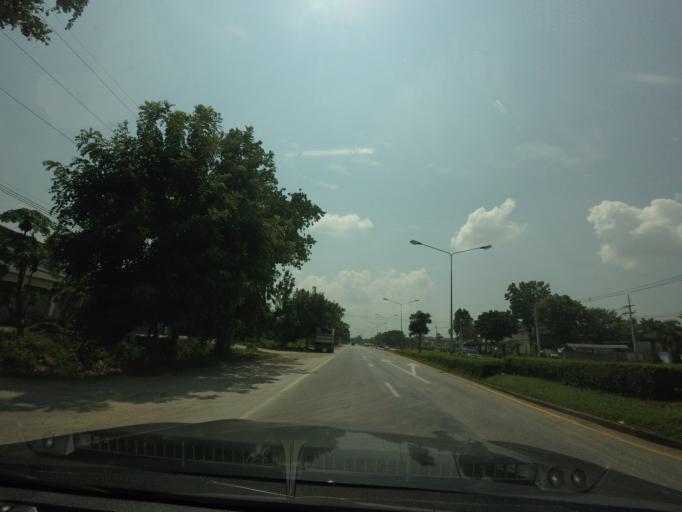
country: TH
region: Uttaradit
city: Uttaradit
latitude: 17.6159
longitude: 100.1240
